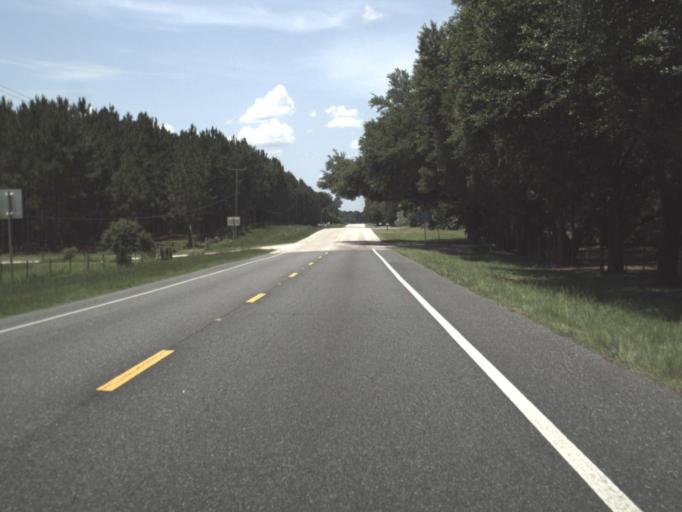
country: US
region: Florida
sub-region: Gilchrist County
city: Trenton
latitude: 29.5833
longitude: -82.8232
